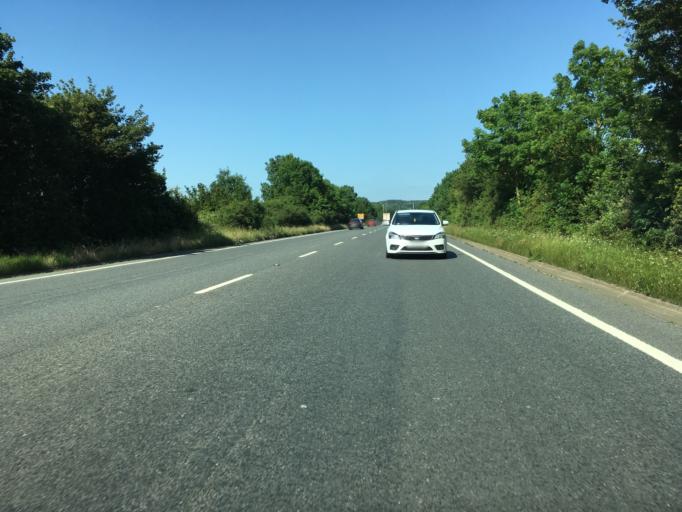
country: GB
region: England
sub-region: Milton Keynes
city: Water Eaton
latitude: 51.9818
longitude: -0.7066
